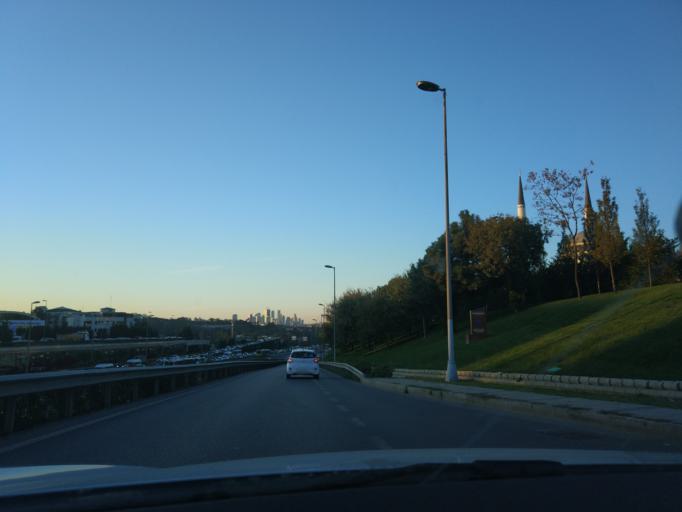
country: TR
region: Istanbul
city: UEskuedar
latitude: 41.0236
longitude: 29.0478
